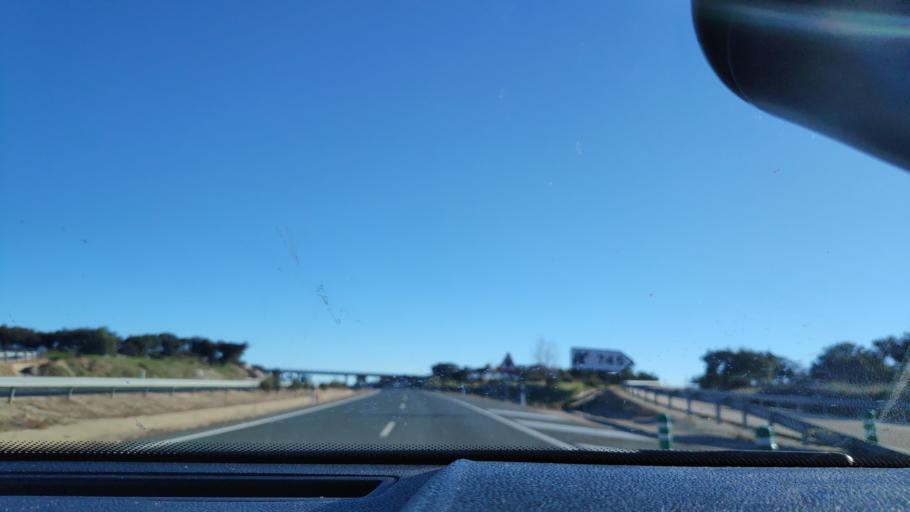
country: ES
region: Andalusia
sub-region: Provincia de Huelva
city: Santa Olalla del Cala
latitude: 37.9205
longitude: -6.2255
